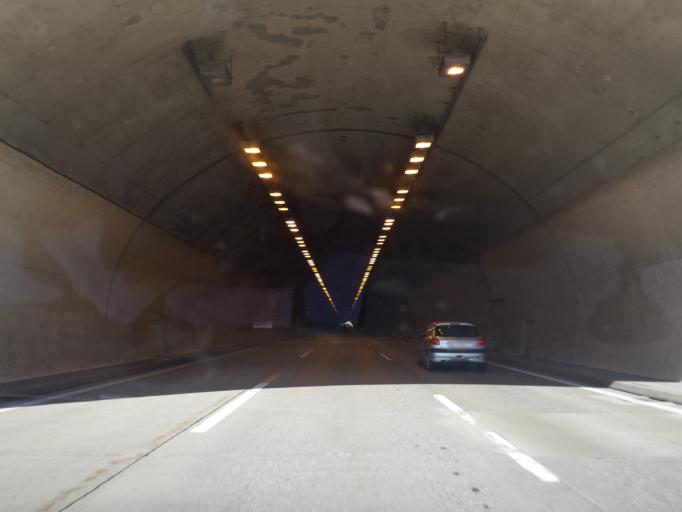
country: AT
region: Styria
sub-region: Politischer Bezirk Graz-Umgebung
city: Gratkorn
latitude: 47.1413
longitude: 15.3442
